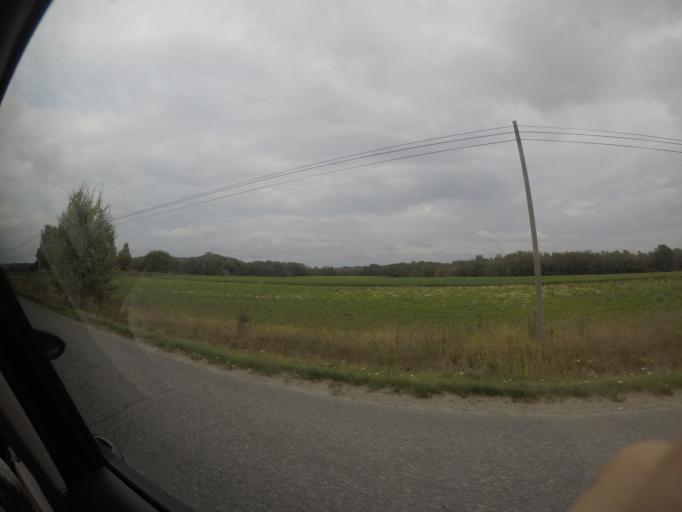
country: FI
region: Haeme
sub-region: Haemeenlinna
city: Haemeenlinna
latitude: 61.0314
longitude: 24.4169
